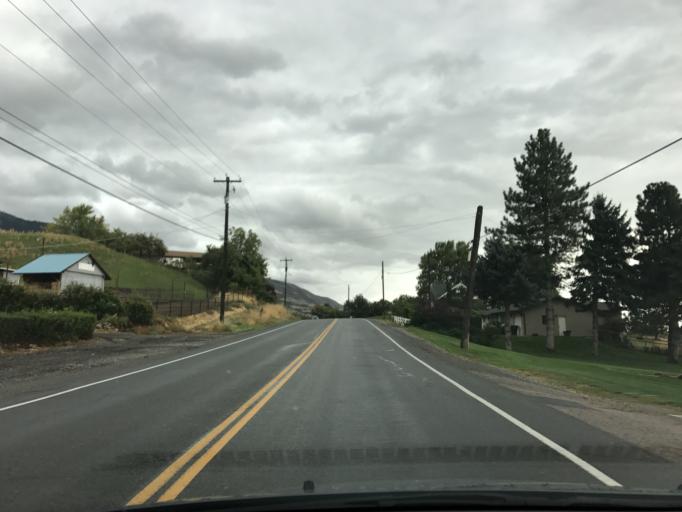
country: US
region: Utah
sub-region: Davis County
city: Farmington
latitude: 40.9972
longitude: -111.8977
